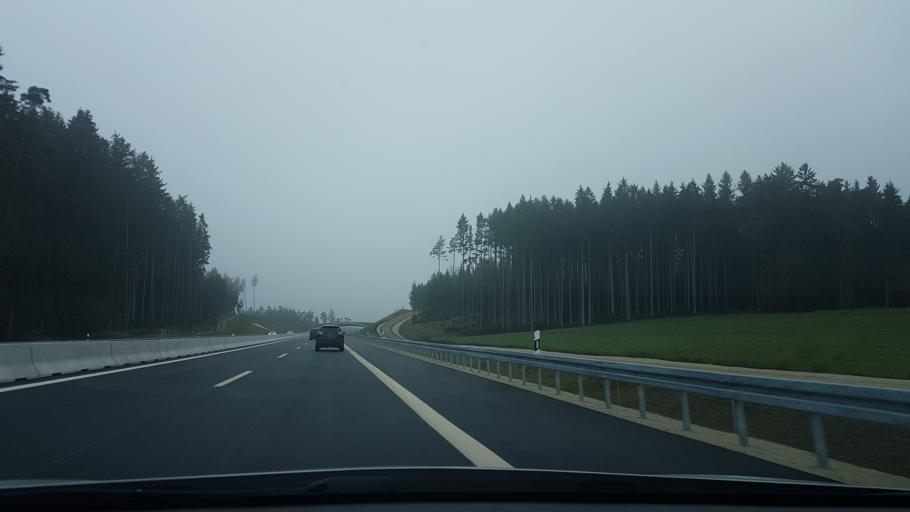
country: DE
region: Bavaria
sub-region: Lower Bavaria
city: Buch
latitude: 48.6493
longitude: 12.1938
